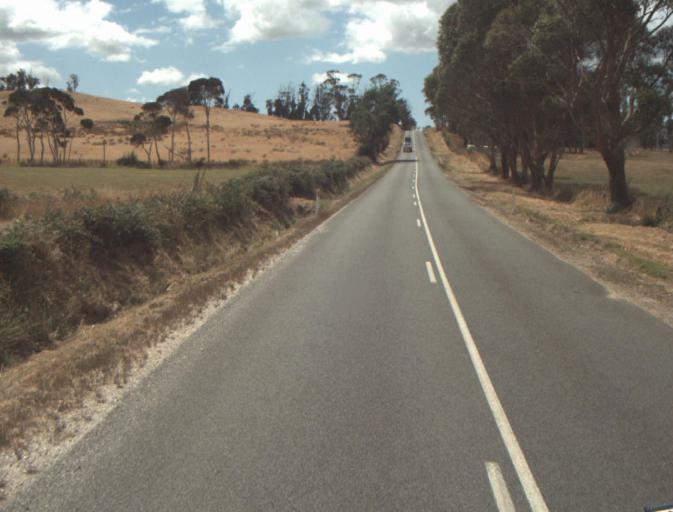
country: AU
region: Tasmania
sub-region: Launceston
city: Mayfield
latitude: -41.2233
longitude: 147.1217
